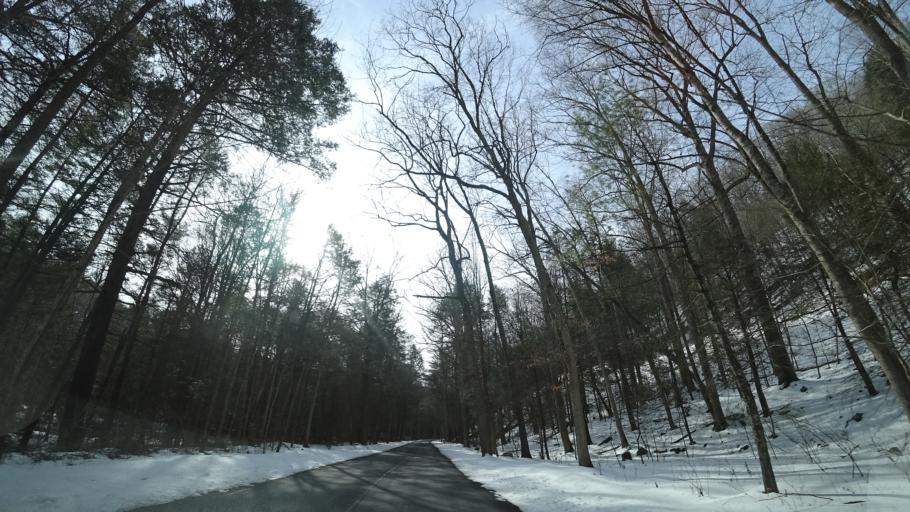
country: US
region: Virginia
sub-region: Shenandoah County
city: Woodstock
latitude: 38.9984
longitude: -78.6565
